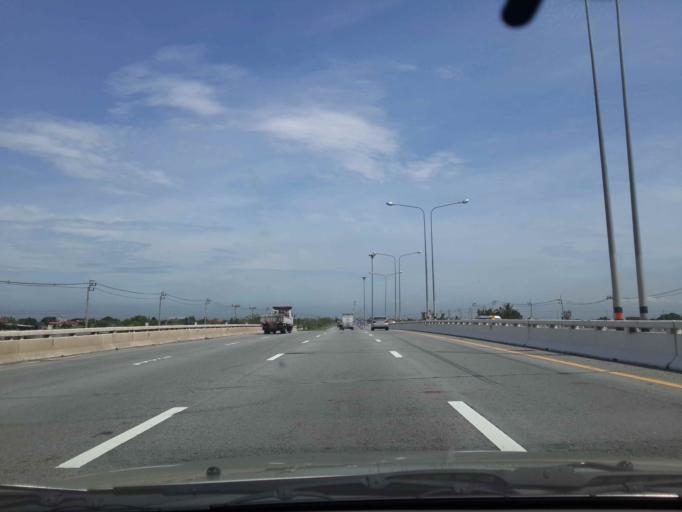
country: TH
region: Samut Prakan
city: Ban Khlong Bang Sao Thong
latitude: 13.6362
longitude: 100.8962
